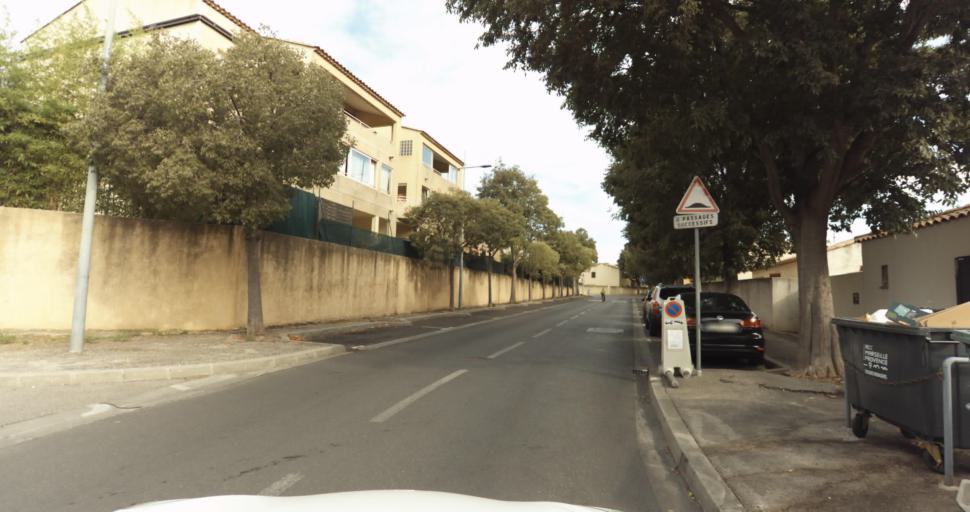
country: FR
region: Provence-Alpes-Cote d'Azur
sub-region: Departement des Bouches-du-Rhone
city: Miramas
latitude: 43.5888
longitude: 5.0097
